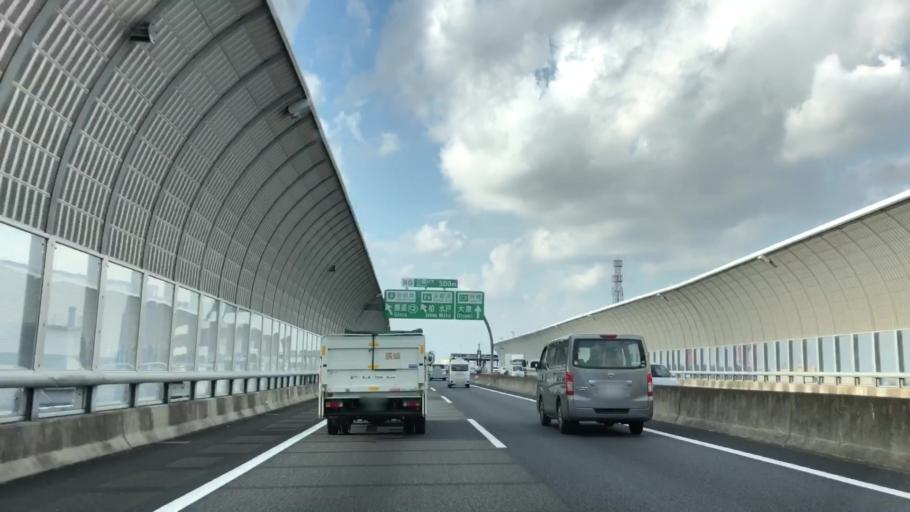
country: JP
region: Saitama
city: Yashio-shi
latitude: 35.8290
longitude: 139.8676
